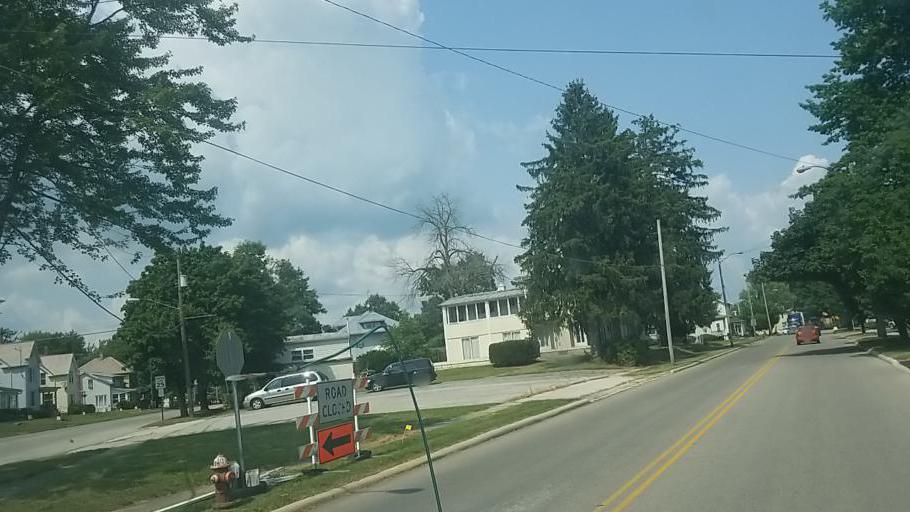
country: US
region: Ohio
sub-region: Crawford County
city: Bucyrus
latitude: 40.7980
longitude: -82.9769
